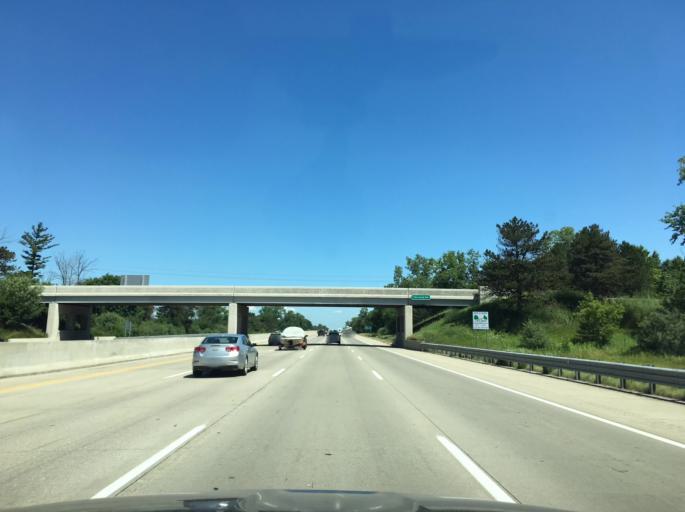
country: US
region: Michigan
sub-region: Genesee County
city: Clio
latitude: 43.1911
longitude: -83.7688
